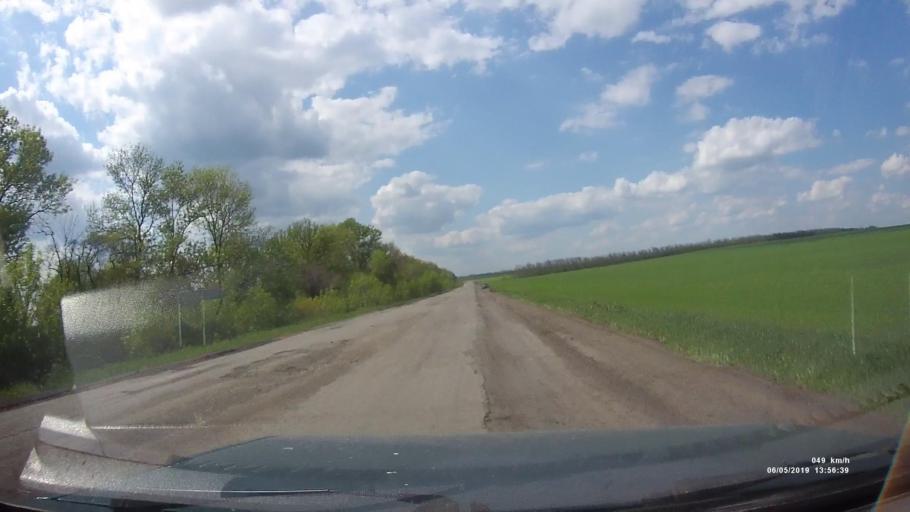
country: RU
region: Rostov
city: Melikhovskaya
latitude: 47.6819
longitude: 40.4293
